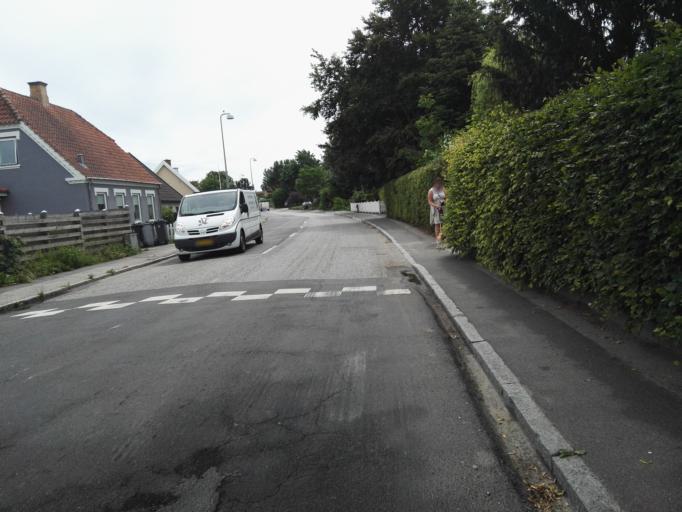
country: DK
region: Capital Region
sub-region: Hillerod Kommune
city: Skaevinge
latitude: 55.9055
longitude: 12.1504
